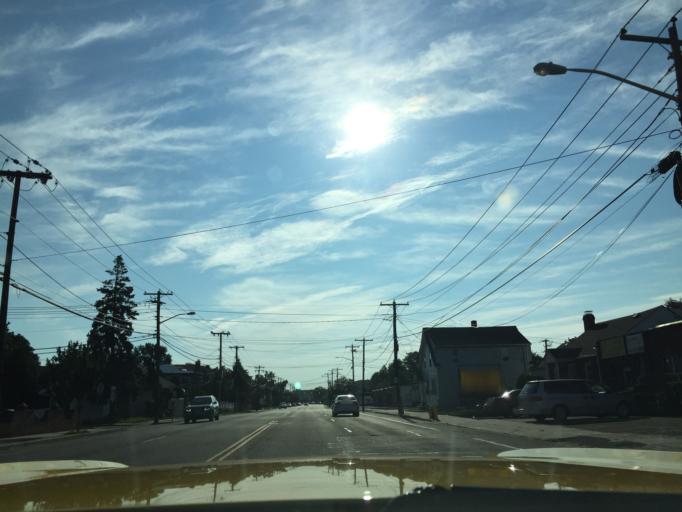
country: US
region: New York
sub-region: Nassau County
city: Hicksville
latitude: 40.7668
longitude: -73.5392
